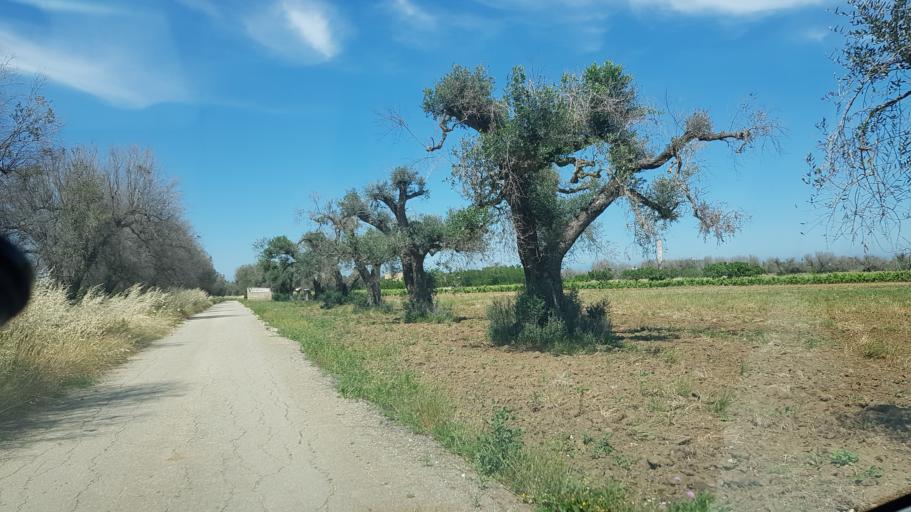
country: IT
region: Apulia
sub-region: Provincia di Brindisi
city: Tuturano
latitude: 40.5400
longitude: 17.9976
